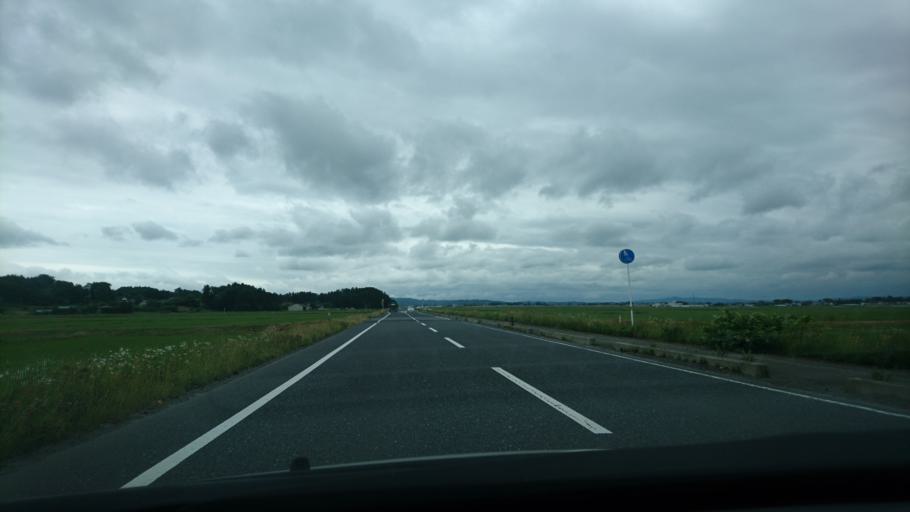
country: JP
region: Miyagi
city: Wakuya
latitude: 38.7020
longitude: 141.2602
